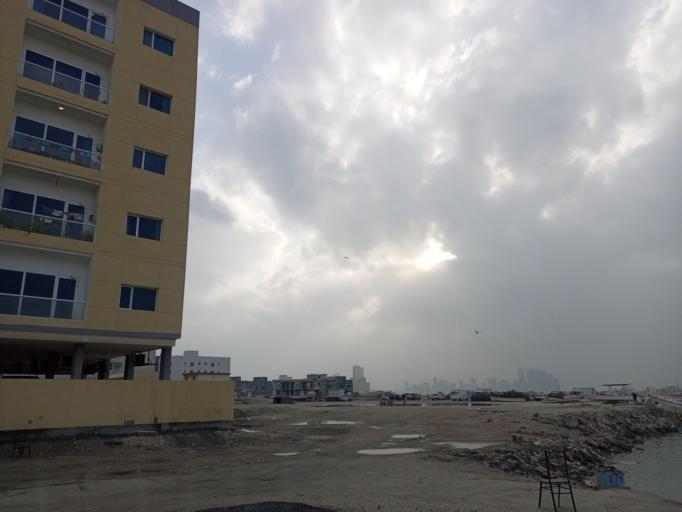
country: BH
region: Muharraq
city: Al Hadd
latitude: 26.2421
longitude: 50.6455
